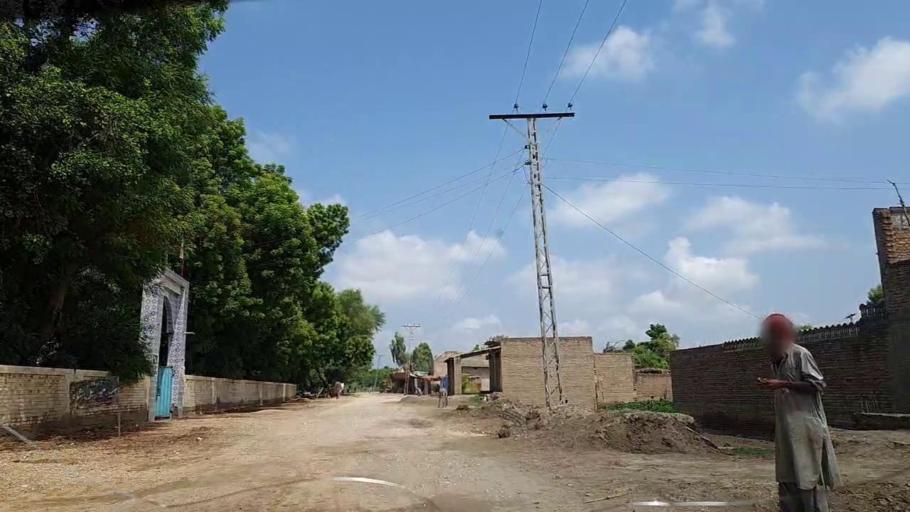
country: PK
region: Sindh
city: Tharu Shah
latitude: 26.9111
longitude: 68.0341
